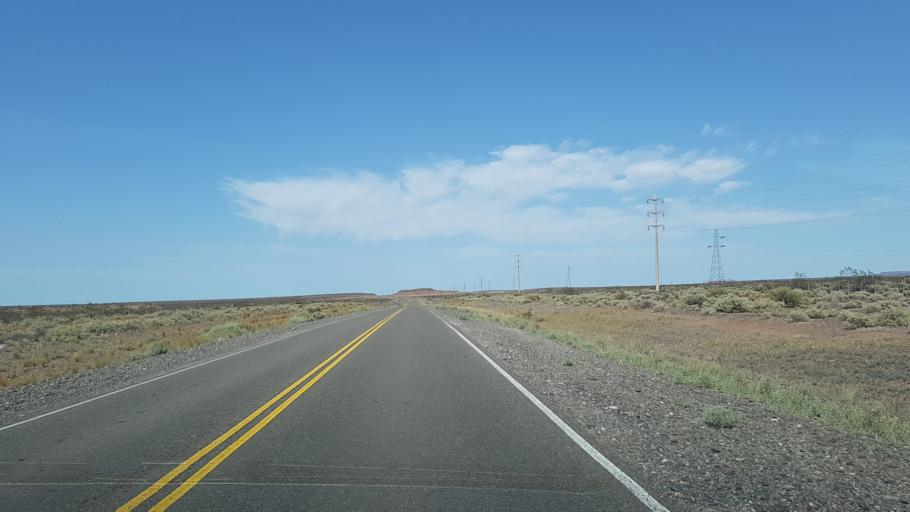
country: AR
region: Neuquen
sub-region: Departamento de Picun Leufu
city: Picun Leufu
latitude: -39.3947
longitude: -69.1117
